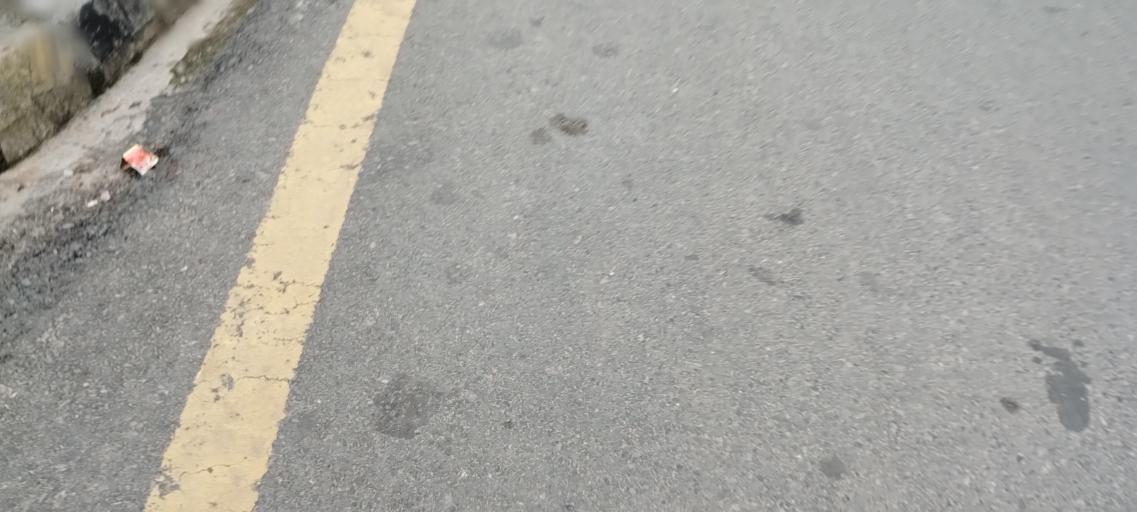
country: NP
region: Central Region
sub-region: Bagmati Zone
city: Kathmandu
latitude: 27.7793
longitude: 85.3633
